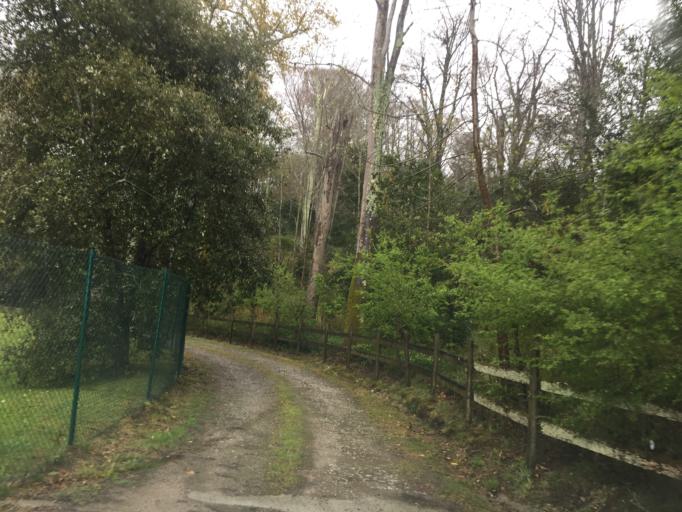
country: ES
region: Cantabria
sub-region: Provincia de Cantabria
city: Comillas
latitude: 43.3835
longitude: -4.2951
